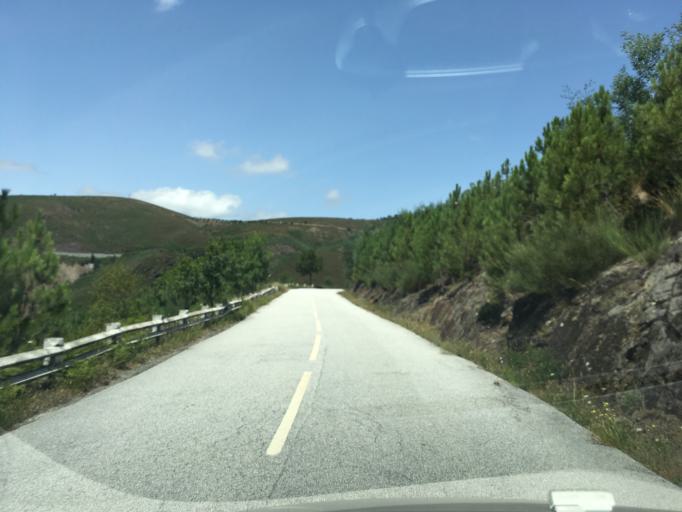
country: PT
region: Vila Real
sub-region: Mesao Frio
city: Mesao Frio
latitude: 41.2653
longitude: -7.9335
